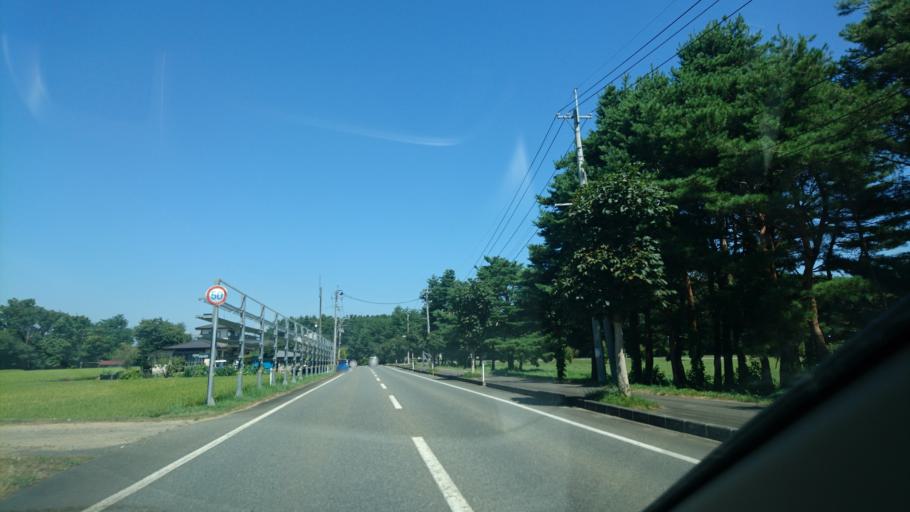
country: JP
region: Iwate
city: Kitakami
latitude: 39.2607
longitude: 141.0864
